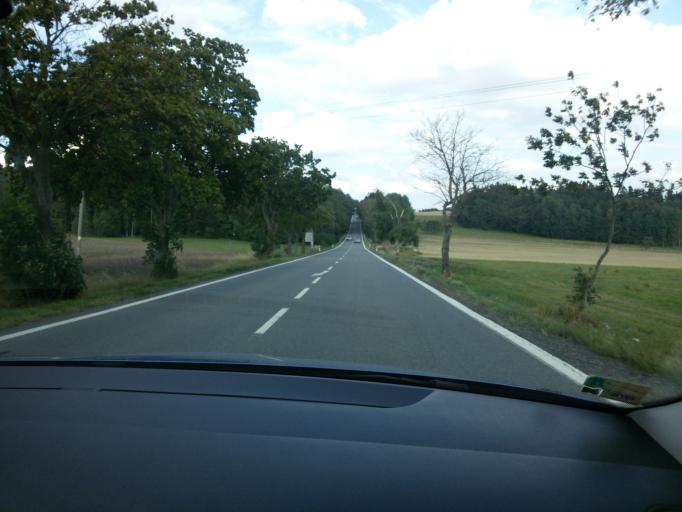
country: CZ
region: Pardubicky
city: Prosec
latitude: 49.7403
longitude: 16.1742
